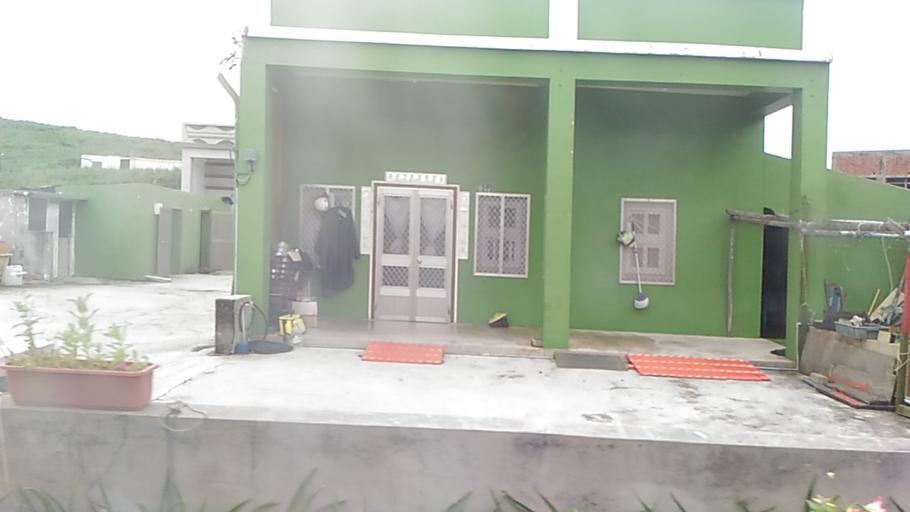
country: TW
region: Taiwan
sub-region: Penghu
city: Ma-kung
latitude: 23.2106
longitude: 119.4368
